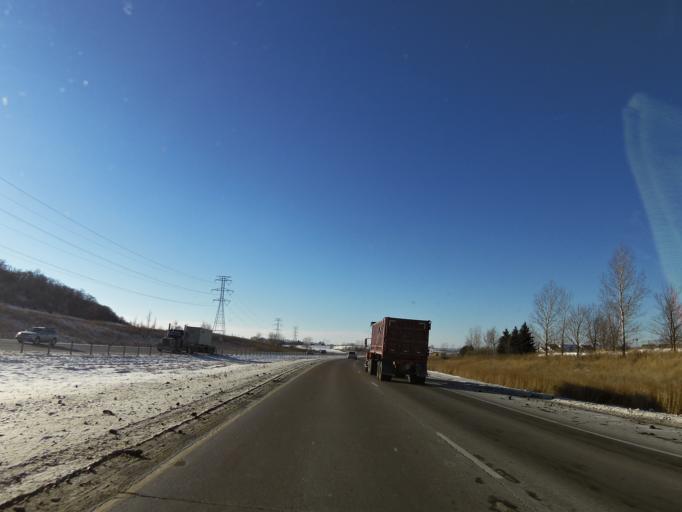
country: US
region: Minnesota
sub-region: Scott County
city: Shakopee
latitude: 44.7762
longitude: -93.5457
